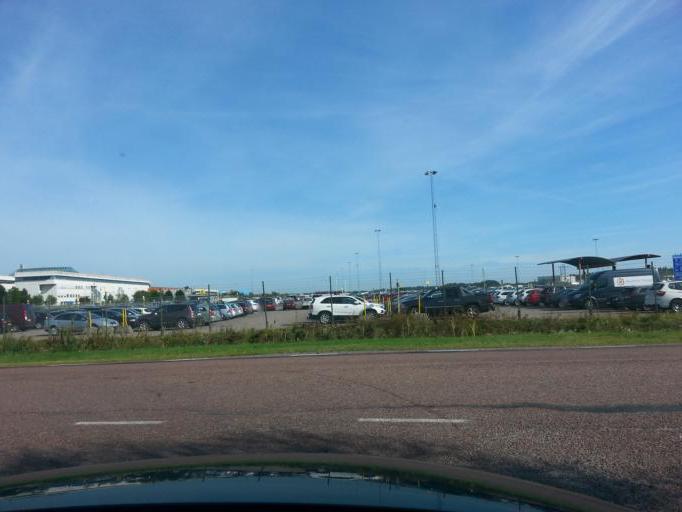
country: SE
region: Stockholm
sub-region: Sigtuna Kommun
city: Rosersberg
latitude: 59.6377
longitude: 17.9429
